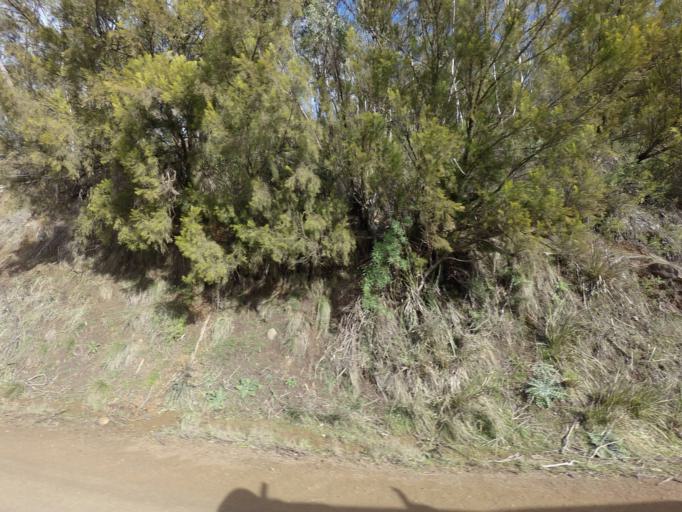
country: AU
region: Tasmania
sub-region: Derwent Valley
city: New Norfolk
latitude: -42.7898
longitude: 146.9392
